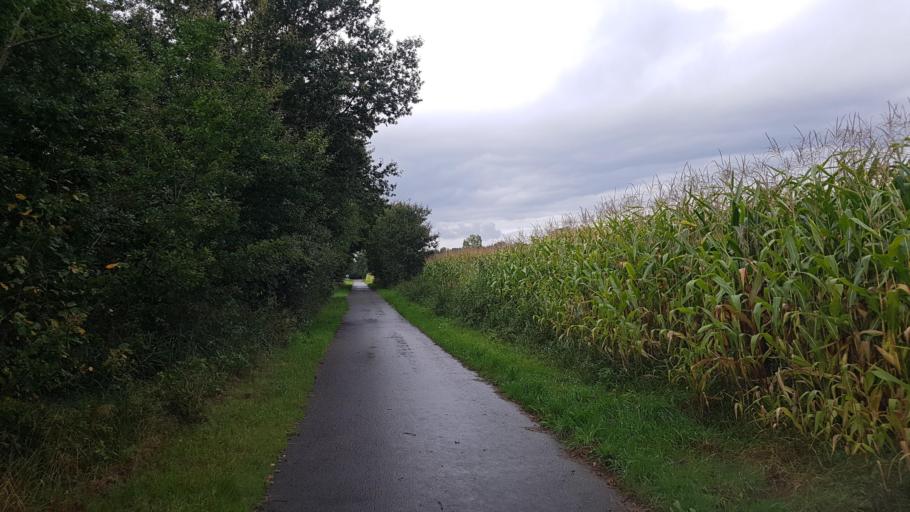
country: DE
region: Brandenburg
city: Schraden
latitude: 51.4623
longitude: 13.7161
